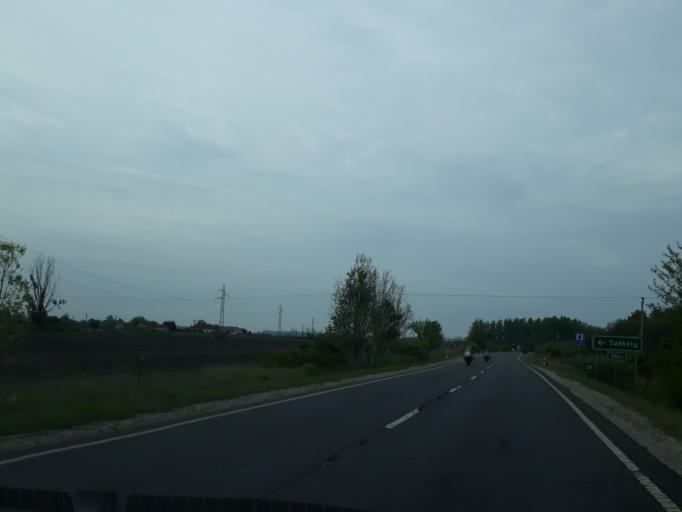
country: HU
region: Szabolcs-Szatmar-Bereg
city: Nyirbogdany
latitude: 48.0640
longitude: 21.9293
